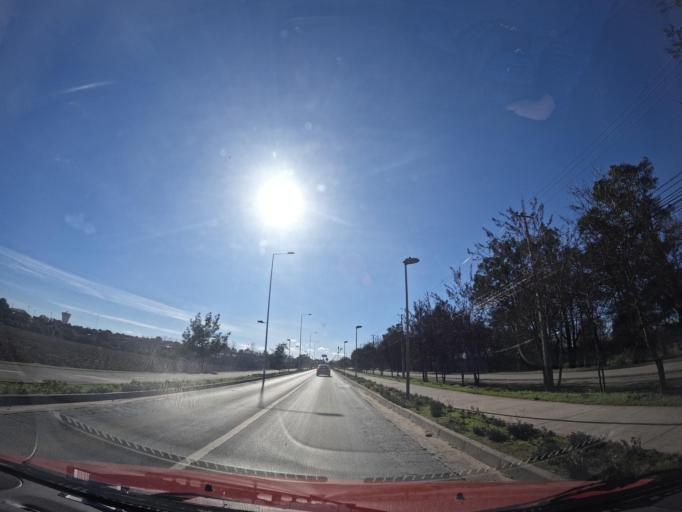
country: CL
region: Maule
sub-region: Provincia de Cauquenes
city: Cauquenes
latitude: -35.9768
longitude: -72.3153
